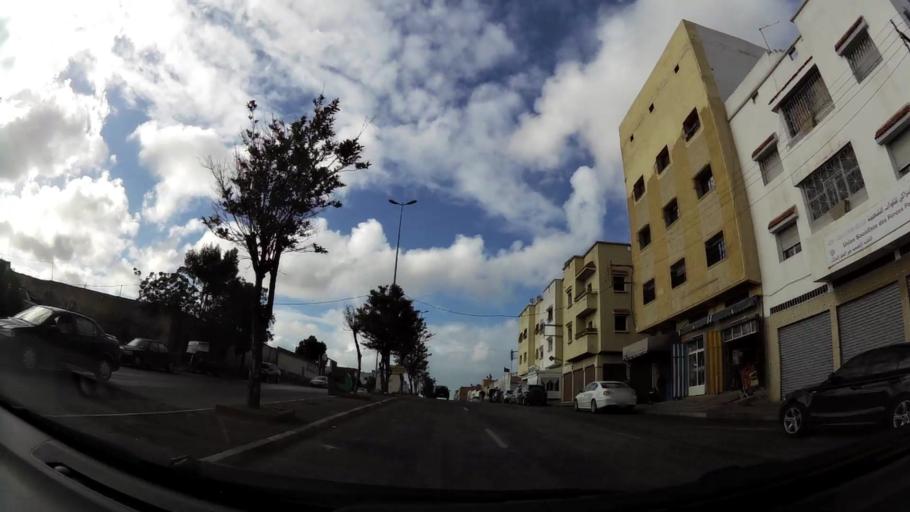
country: MA
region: Grand Casablanca
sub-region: Casablanca
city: Casablanca
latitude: 33.5448
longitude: -7.5889
